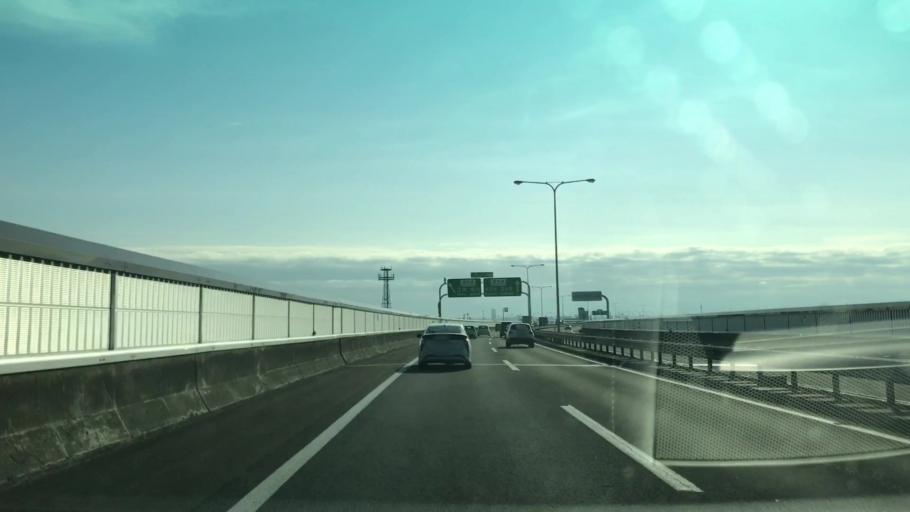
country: JP
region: Hokkaido
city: Sapporo
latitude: 43.0883
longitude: 141.4146
